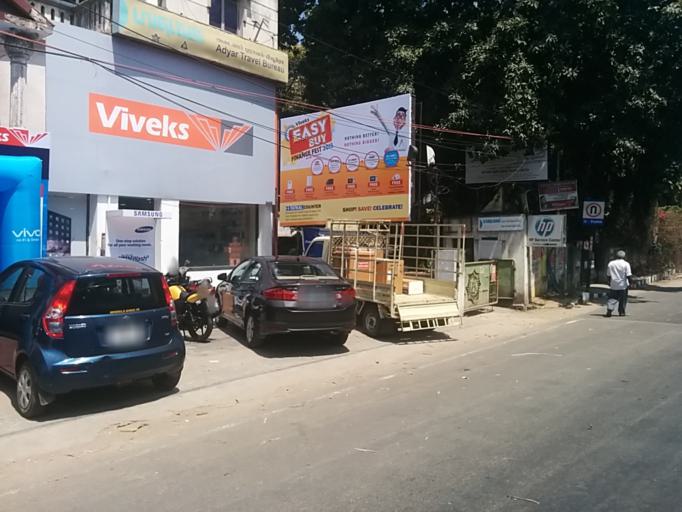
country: IN
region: Tamil Nadu
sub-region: Chennai
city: Gandhi Nagar
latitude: 13.0067
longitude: 80.2566
